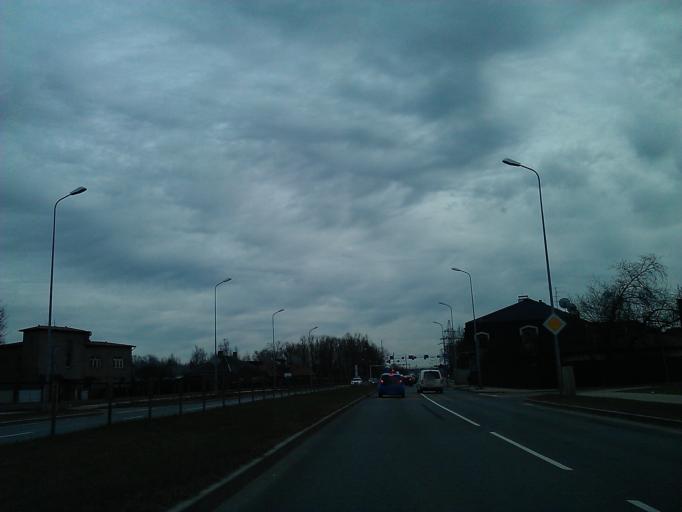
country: LV
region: Riga
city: Riga
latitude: 56.9412
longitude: 24.1704
